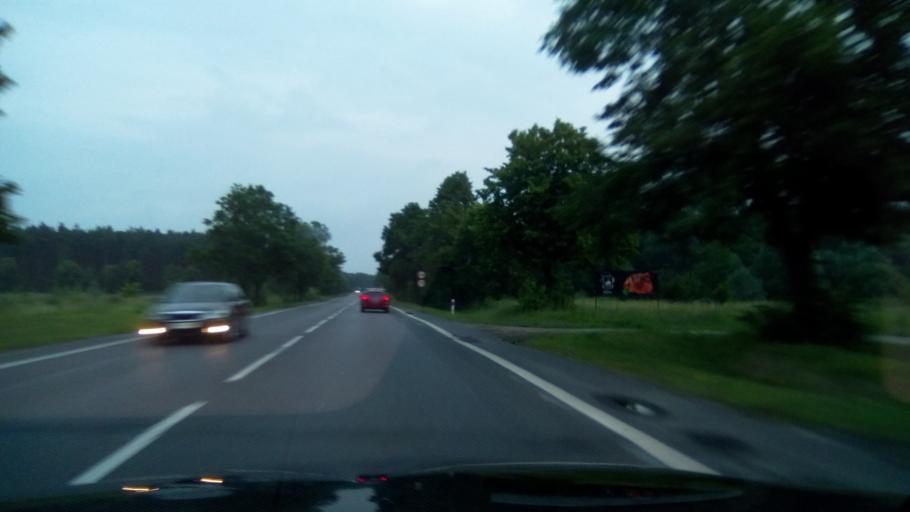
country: PL
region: Greater Poland Voivodeship
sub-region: Powiat poznanski
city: Kobylnica
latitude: 52.4673
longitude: 17.1561
